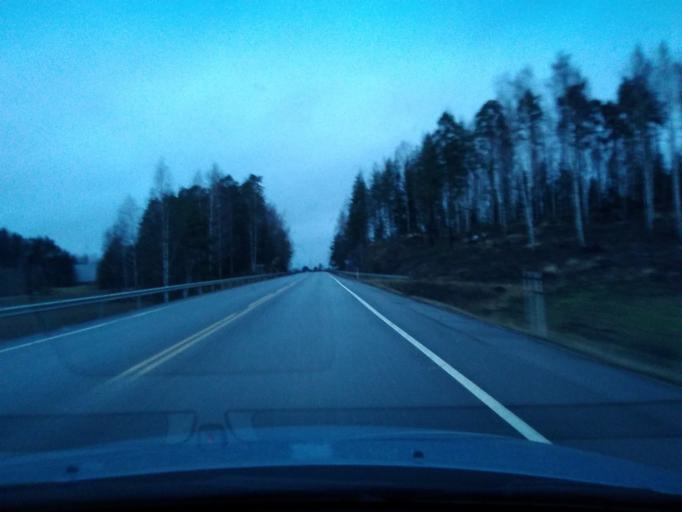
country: FI
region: Uusimaa
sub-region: Porvoo
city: Askola
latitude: 60.4903
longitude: 25.5565
